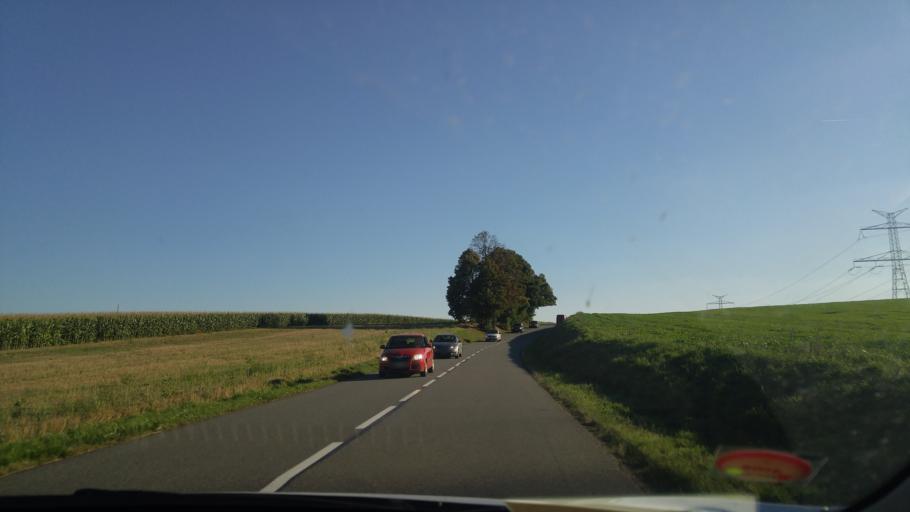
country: CZ
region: South Moravian
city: Ricany
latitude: 49.2309
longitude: 16.4251
